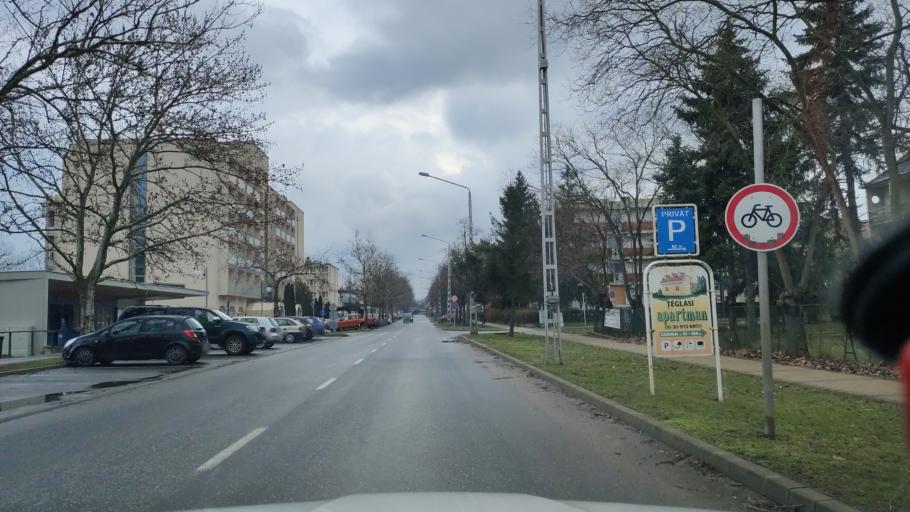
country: HU
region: Hajdu-Bihar
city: Hajduszoboszlo
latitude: 47.4515
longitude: 21.3959
